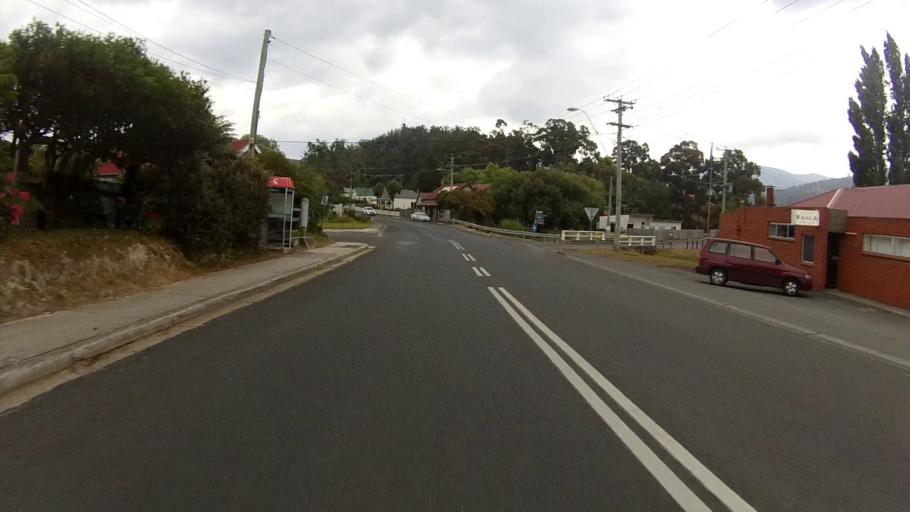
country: AU
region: Tasmania
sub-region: Huon Valley
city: Cygnet
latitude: -43.1558
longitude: 147.0740
